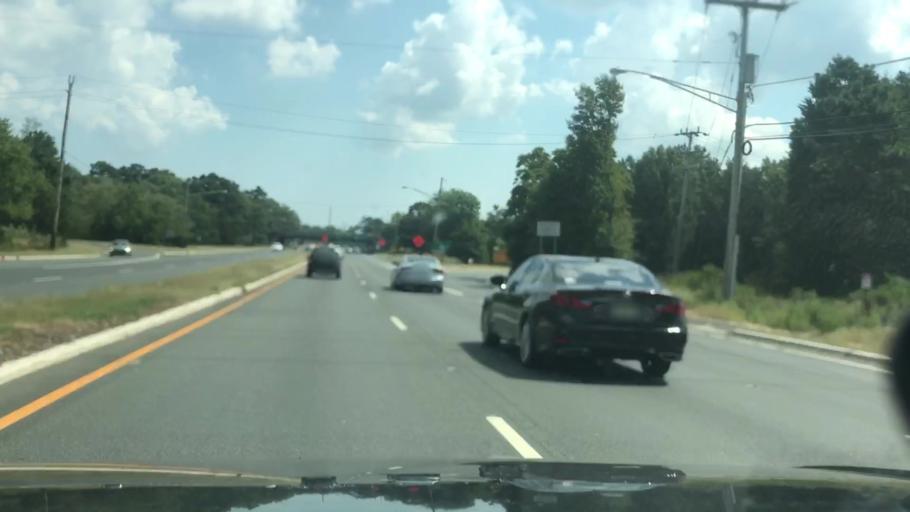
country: US
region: New Jersey
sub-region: Ocean County
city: Silver Ridge
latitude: 39.9645
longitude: -74.2103
